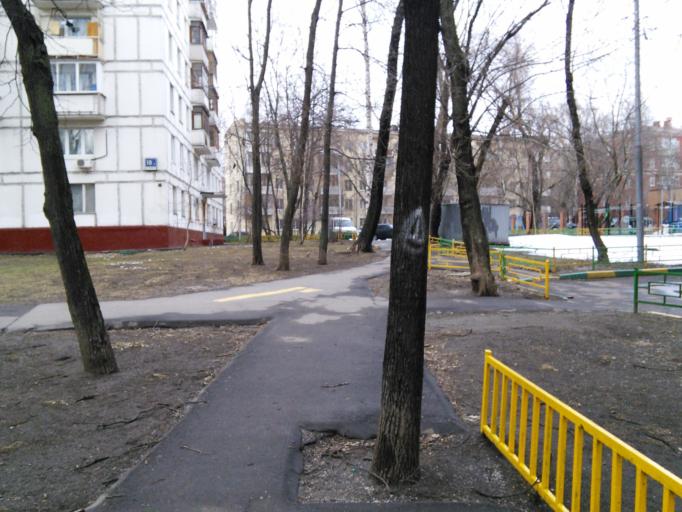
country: RU
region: Moscow
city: Lefortovo
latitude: 55.7668
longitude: 37.7131
